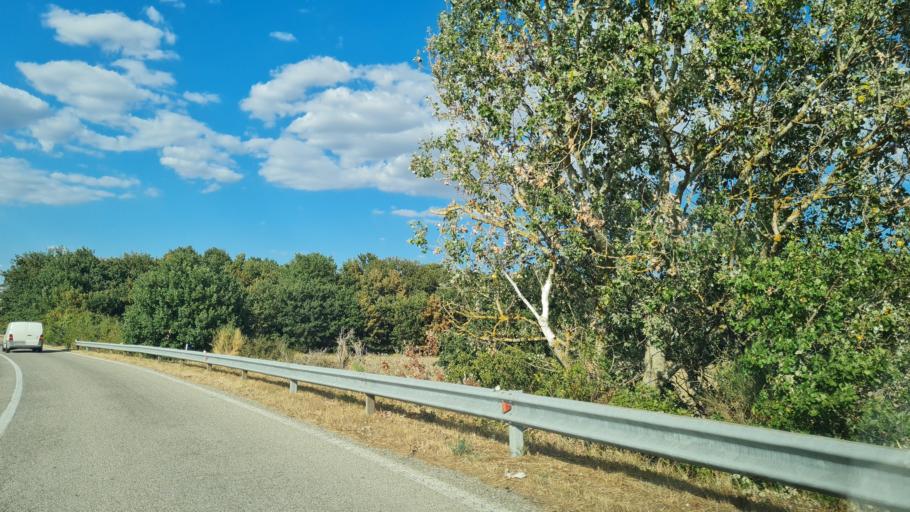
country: IT
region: Tuscany
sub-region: Provincia di Siena
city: Castiglione d'Orcia
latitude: 42.9824
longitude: 11.7118
